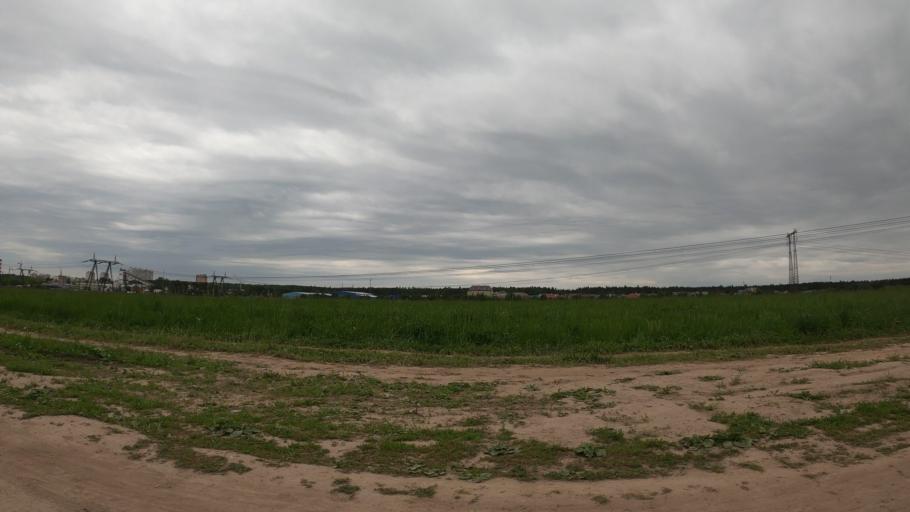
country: RU
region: Moskovskaya
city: Lesnyye Polyany
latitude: 55.9602
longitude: 37.8813
